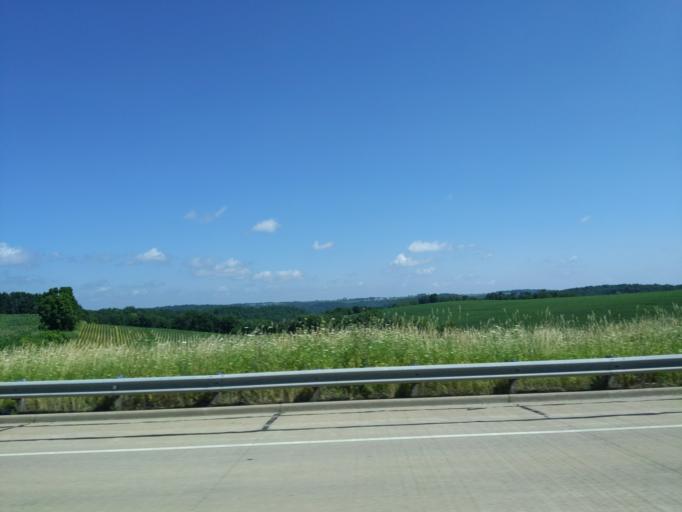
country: US
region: Wisconsin
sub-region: La Crosse County
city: La Crosse
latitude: 43.7325
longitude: -91.1057
